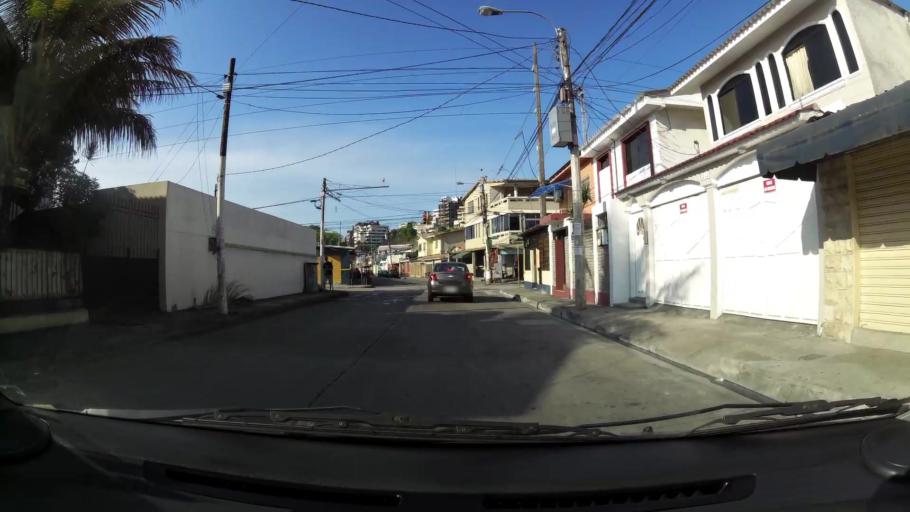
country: EC
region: Guayas
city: Guayaquil
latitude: -2.1602
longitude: -79.9053
